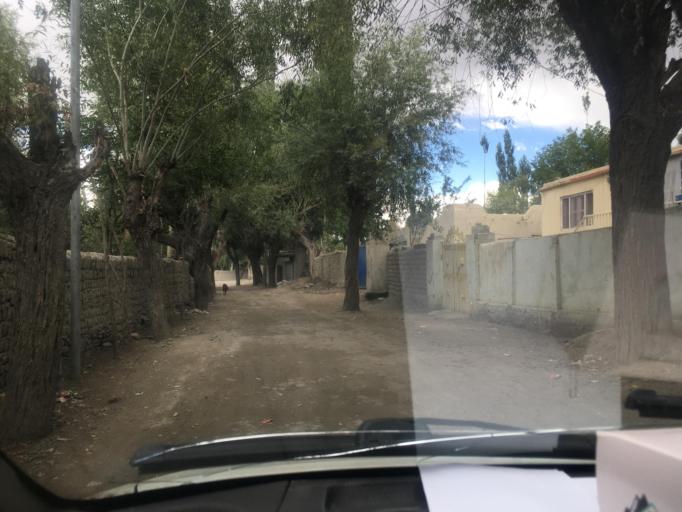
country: PK
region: Gilgit-Baltistan
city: Skardu
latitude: 35.3166
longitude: 75.5489
